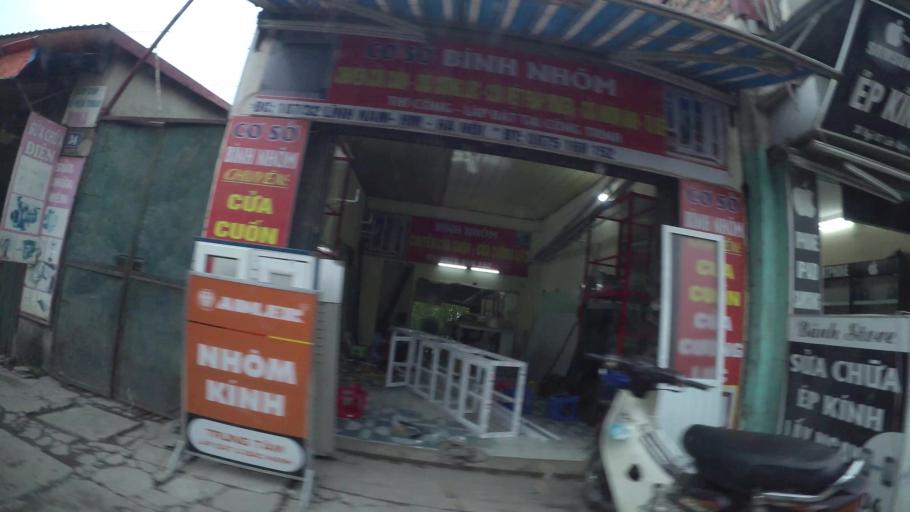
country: VN
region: Ha Noi
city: Hai BaTrung
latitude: 20.9871
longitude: 105.8699
